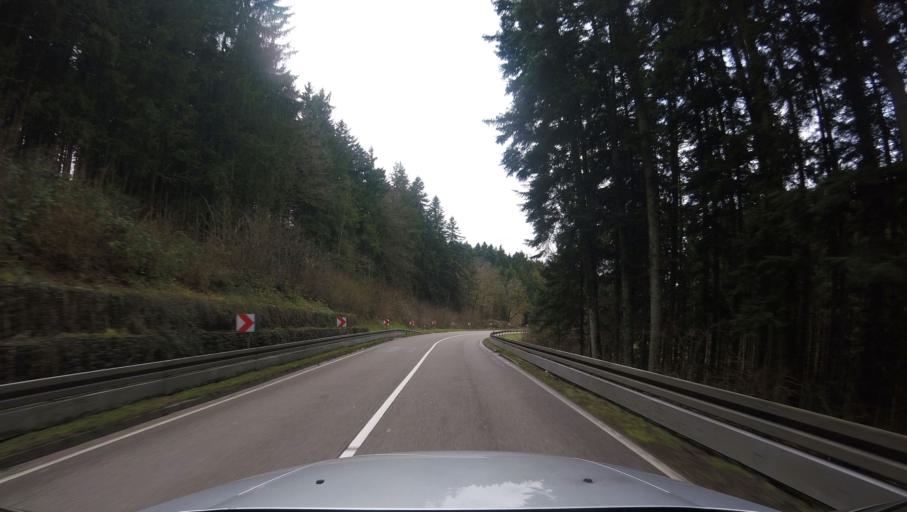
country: DE
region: Baden-Wuerttemberg
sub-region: Regierungsbezirk Stuttgart
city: Durlangen
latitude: 48.8475
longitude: 9.7774
